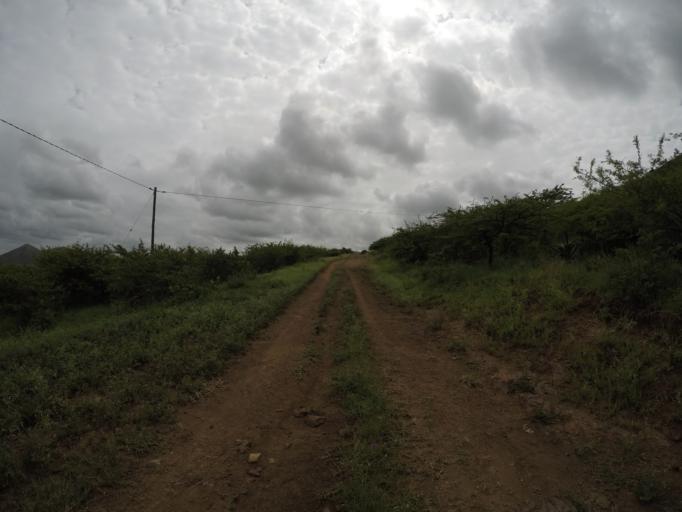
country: ZA
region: KwaZulu-Natal
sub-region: uThungulu District Municipality
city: Empangeni
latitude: -28.6170
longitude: 31.8869
